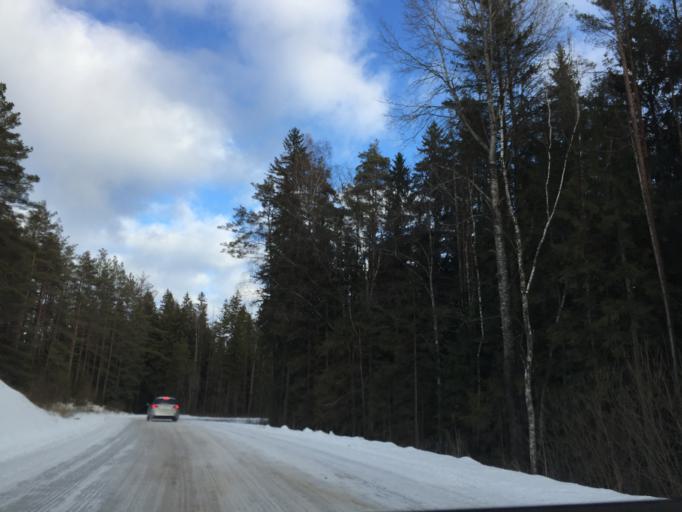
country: LV
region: Ogre
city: Jumprava
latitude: 56.5806
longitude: 24.9520
